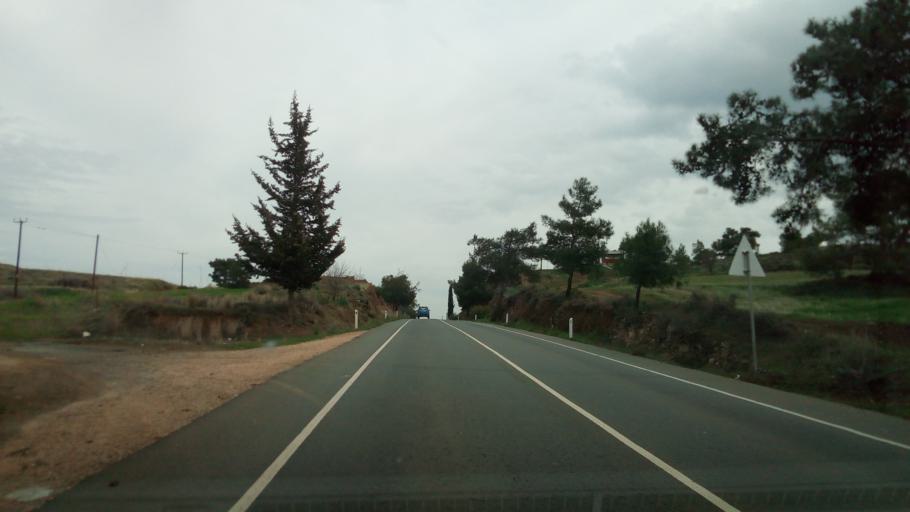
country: CY
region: Lefkosia
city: Kakopetria
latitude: 35.0712
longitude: 32.9372
